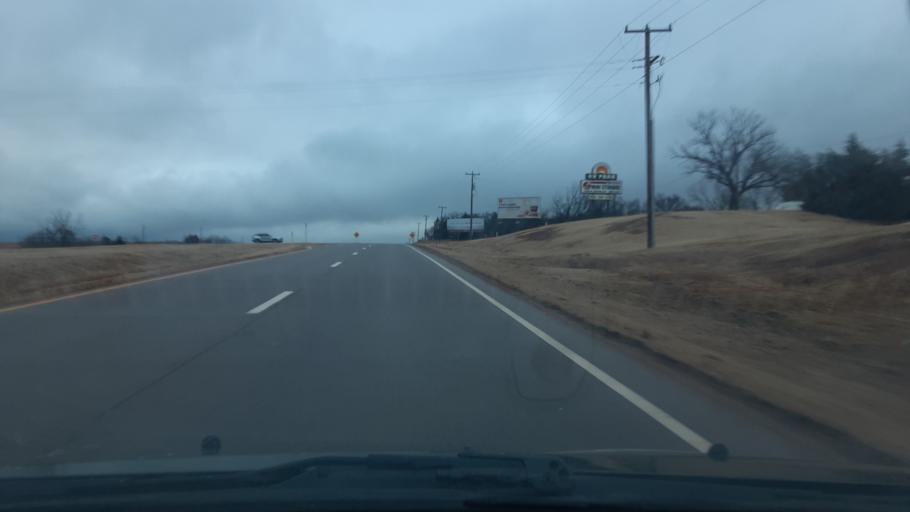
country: US
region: Oklahoma
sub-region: Payne County
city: Stillwater
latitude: 36.1158
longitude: -97.1688
